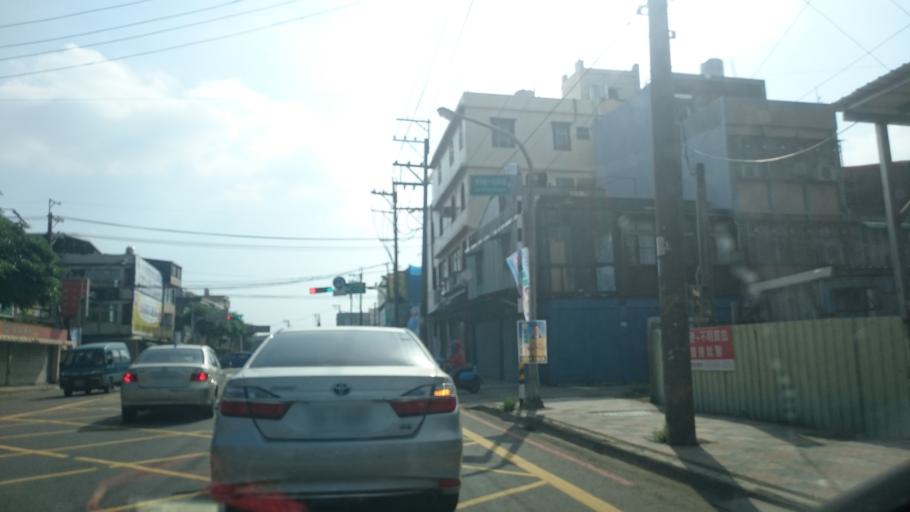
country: TW
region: Taiwan
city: Daxi
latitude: 24.9024
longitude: 121.2744
